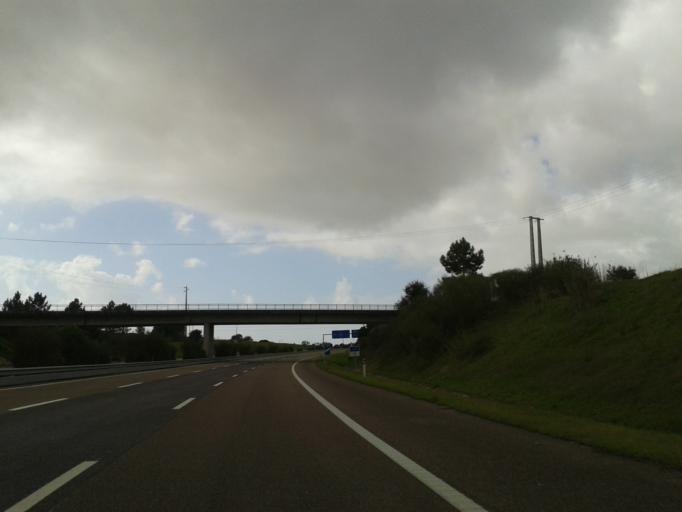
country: PT
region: Setubal
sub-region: Montijo
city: Montijo
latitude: 38.7180
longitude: -8.9300
